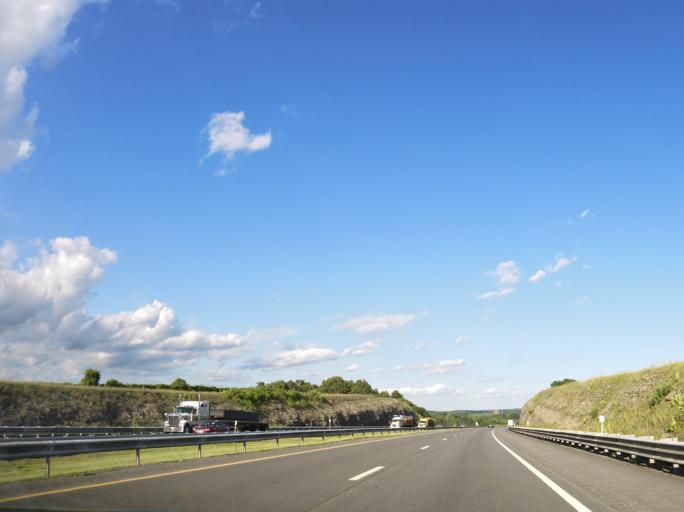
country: US
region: New York
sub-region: Genesee County
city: Batavia
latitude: 43.0223
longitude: -78.1369
